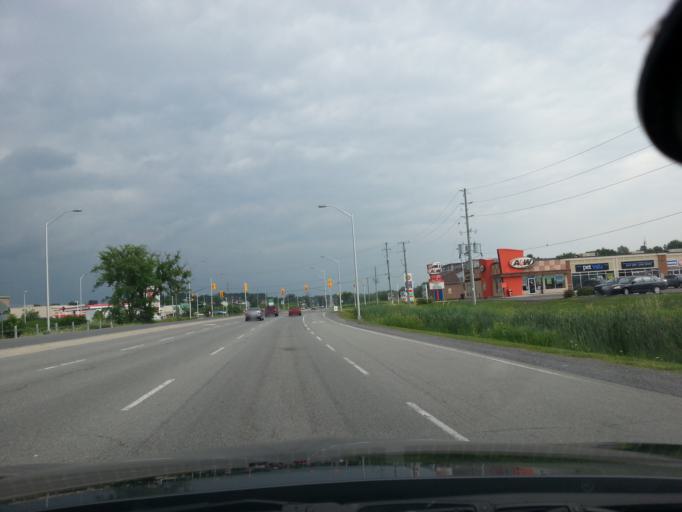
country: CA
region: Ontario
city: Clarence-Rockland
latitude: 45.5448
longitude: -75.3039
